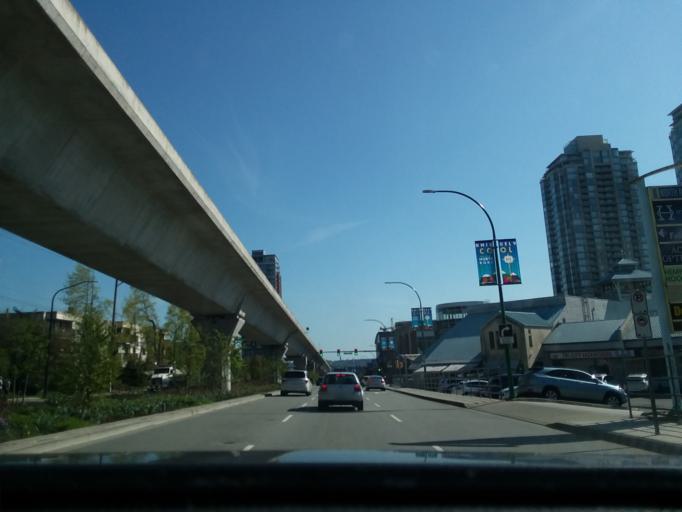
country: CA
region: British Columbia
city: Port Moody
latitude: 49.2543
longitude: -122.8931
